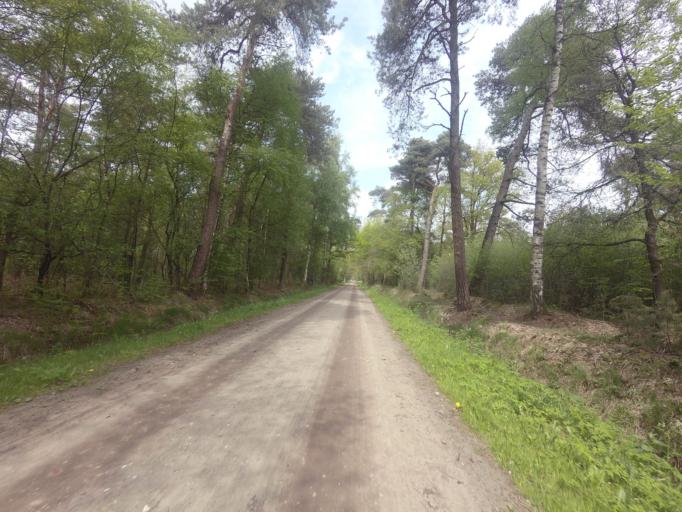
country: NL
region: Overijssel
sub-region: Gemeente Hof van Twente
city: Delden
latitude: 52.2395
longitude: 6.7238
